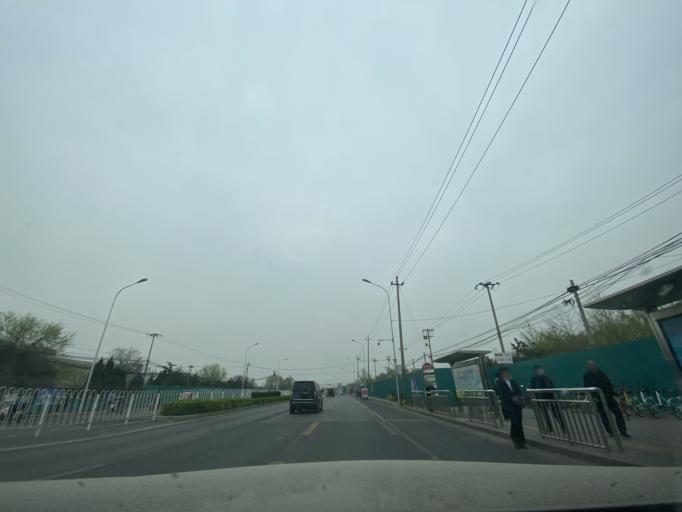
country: CN
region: Beijing
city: Sijiqing
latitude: 39.9455
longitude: 116.2524
